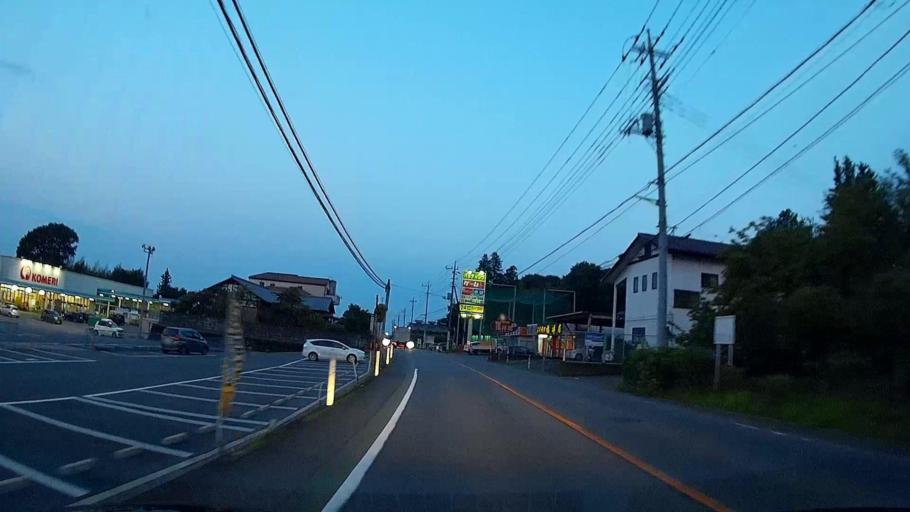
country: JP
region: Gunma
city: Annaka
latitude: 36.3697
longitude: 138.9046
